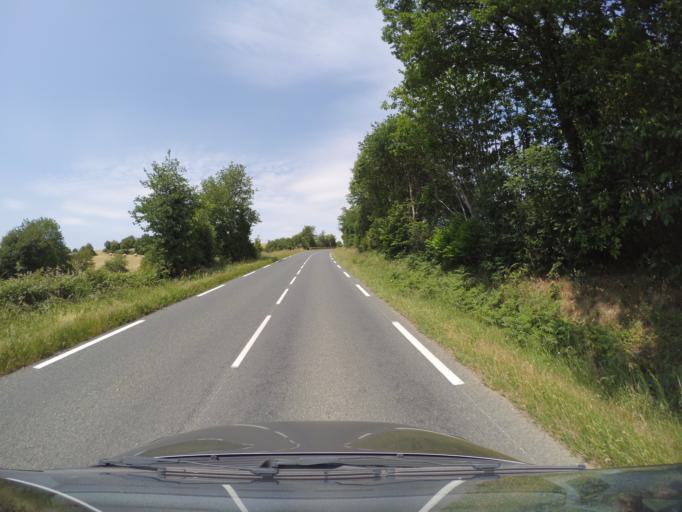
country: FR
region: Pays de la Loire
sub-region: Departement de la Vendee
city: Saint-Michel-Mont-Mercure
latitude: 46.8402
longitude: -0.9121
